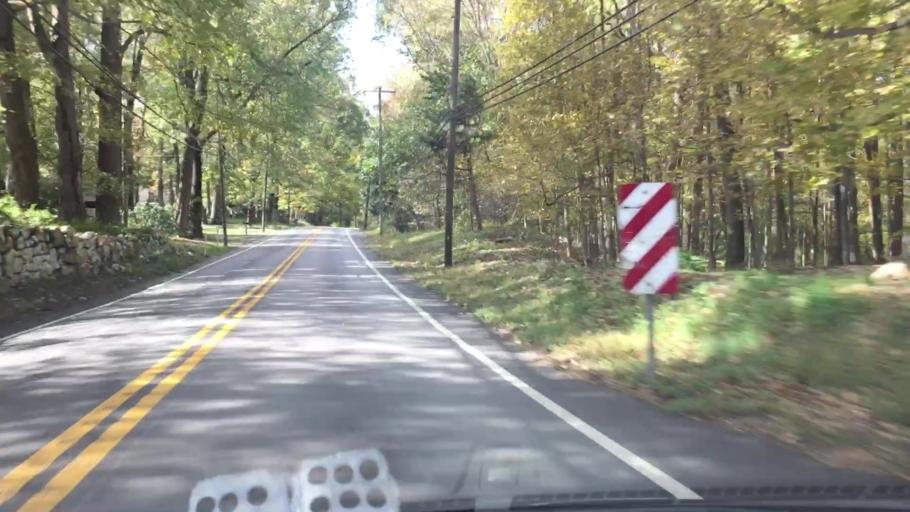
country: US
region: Pennsylvania
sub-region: Delaware County
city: Media
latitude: 39.9459
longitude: -75.4022
